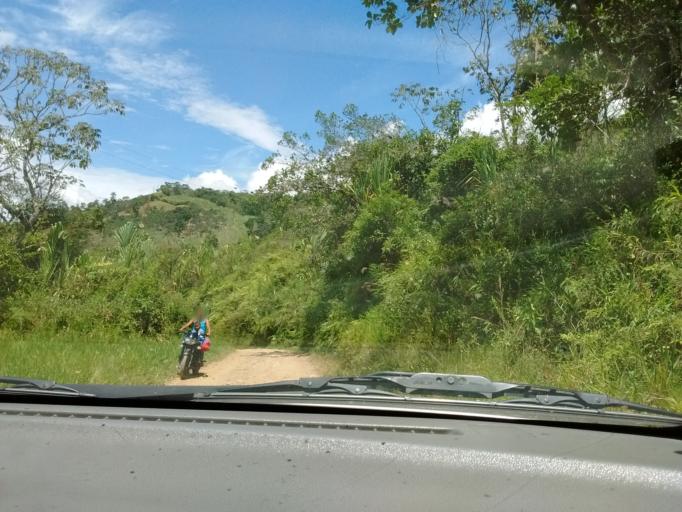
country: CO
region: Cauca
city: Villa Rica
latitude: 2.6371
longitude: -76.7709
